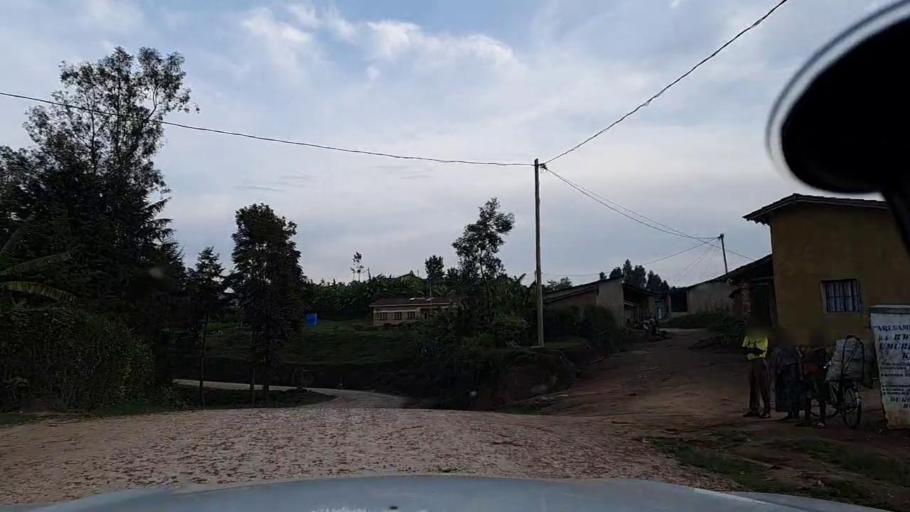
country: RW
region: Southern Province
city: Nyanza
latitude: -2.2139
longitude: 29.6341
